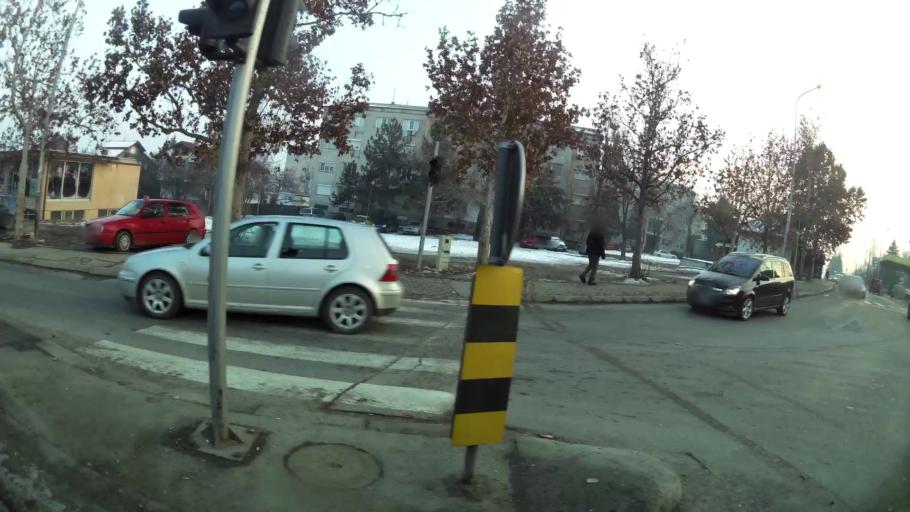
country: MK
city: Creshevo
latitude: 42.0112
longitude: 21.5094
